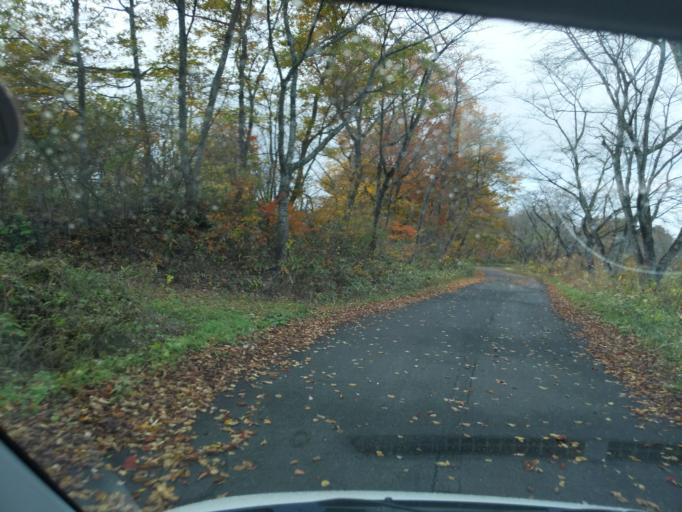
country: JP
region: Iwate
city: Mizusawa
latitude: 39.0564
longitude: 141.0542
